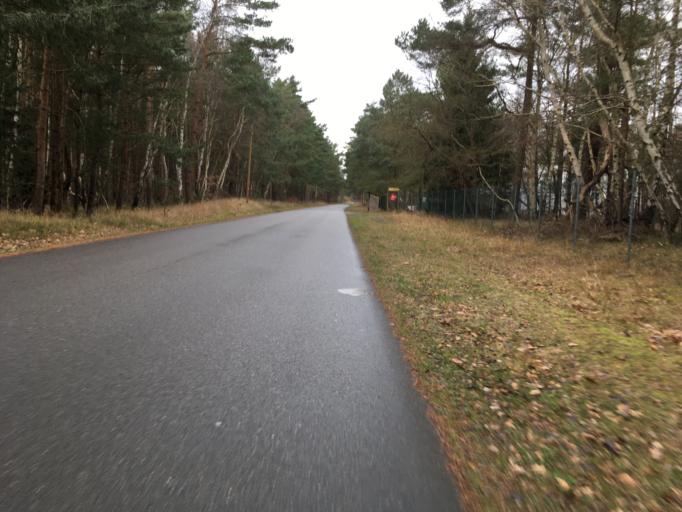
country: DE
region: Mecklenburg-Vorpommern
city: Ostseebad Binz
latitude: 54.4514
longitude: 13.5646
